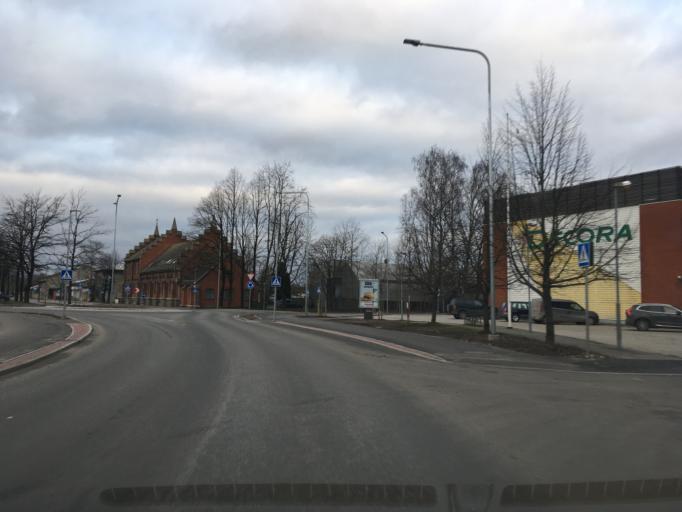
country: EE
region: Paernumaa
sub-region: Paernu linn
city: Parnu
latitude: 58.3879
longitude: 24.5069
